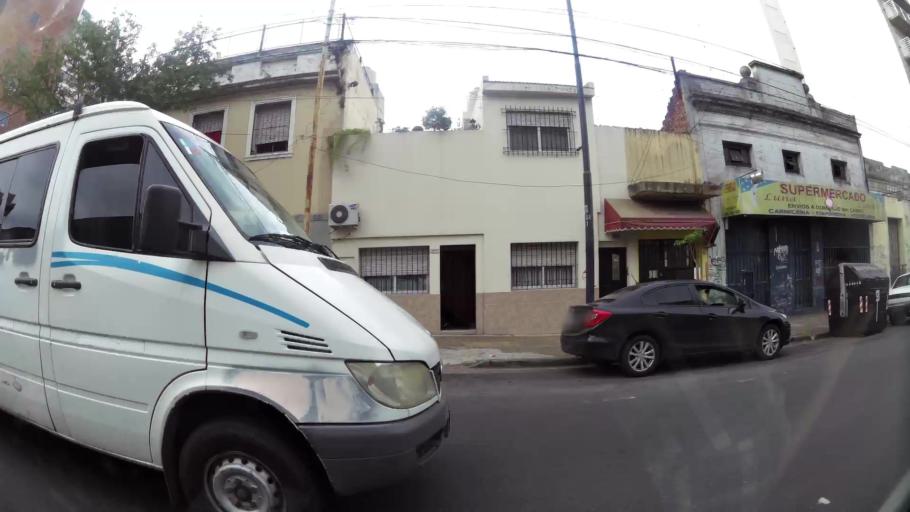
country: AR
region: Buenos Aires F.D.
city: Villa Santa Rita
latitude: -34.6365
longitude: -58.4707
